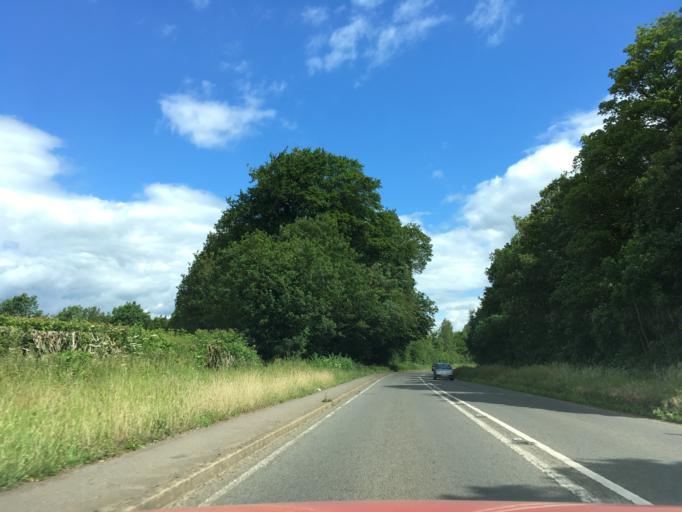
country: GB
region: England
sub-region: Oxfordshire
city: Bloxham
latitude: 52.0430
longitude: -1.3595
